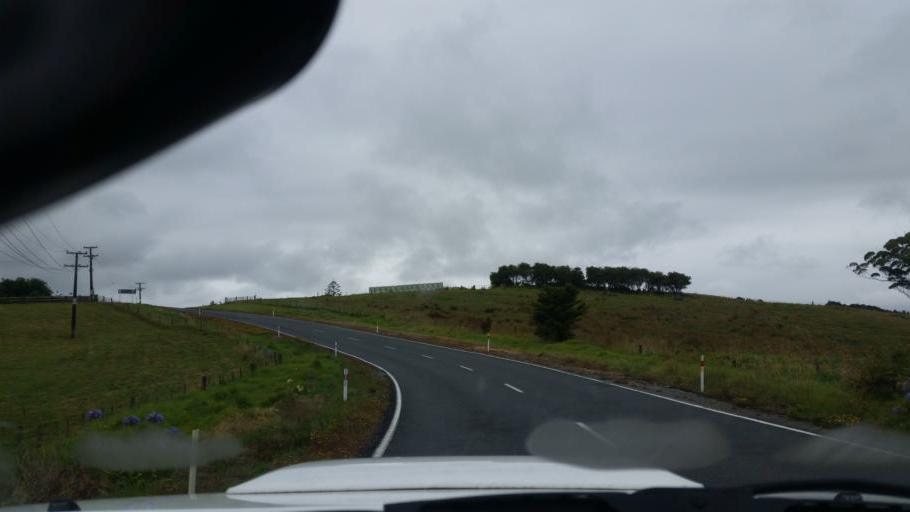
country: NZ
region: Auckland
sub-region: Auckland
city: Wellsford
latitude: -36.1586
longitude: 174.4576
